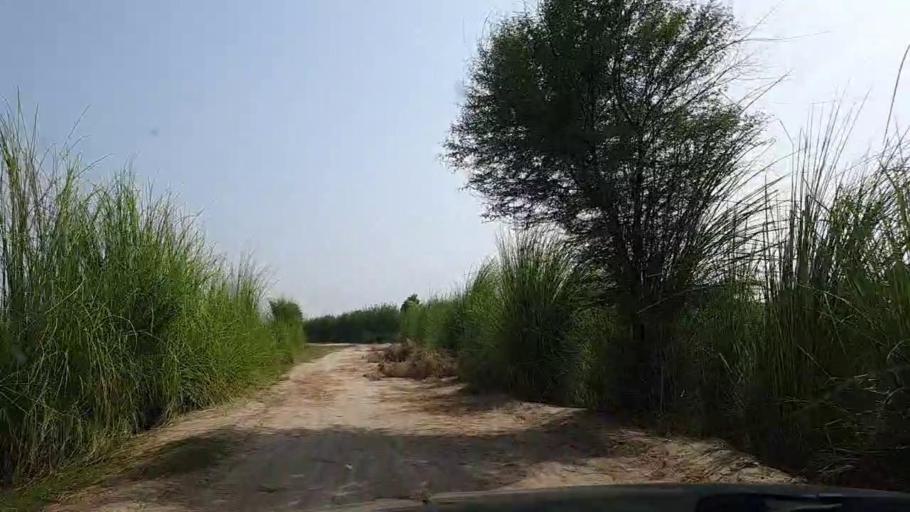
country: PK
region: Sindh
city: Ghotki
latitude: 28.0578
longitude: 69.3800
